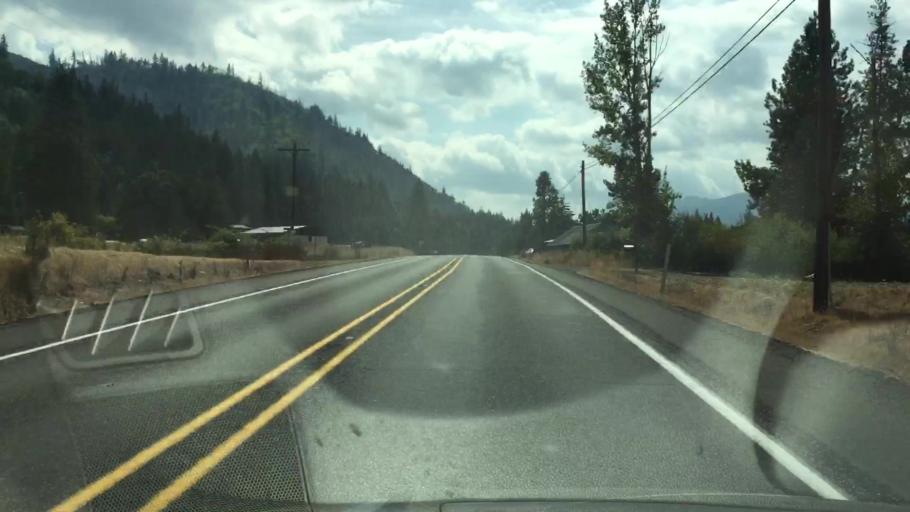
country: US
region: Washington
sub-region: Klickitat County
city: White Salmon
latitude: 45.7923
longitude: -121.4918
